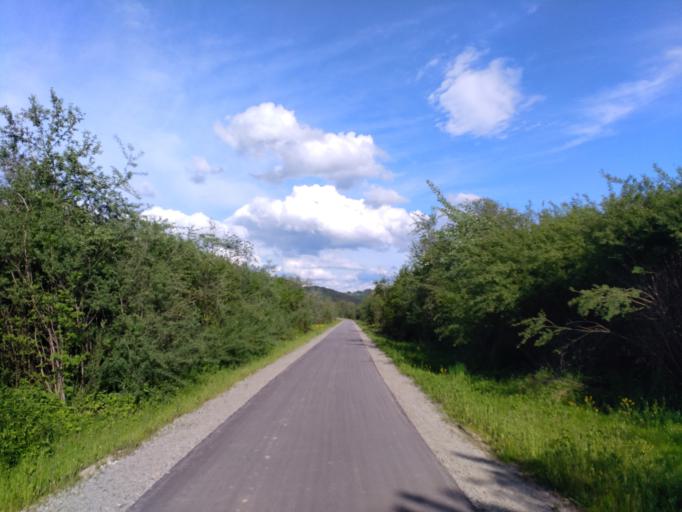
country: PL
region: Lesser Poland Voivodeship
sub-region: Powiat nowosadecki
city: Lacko
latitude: 49.5476
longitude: 20.4530
